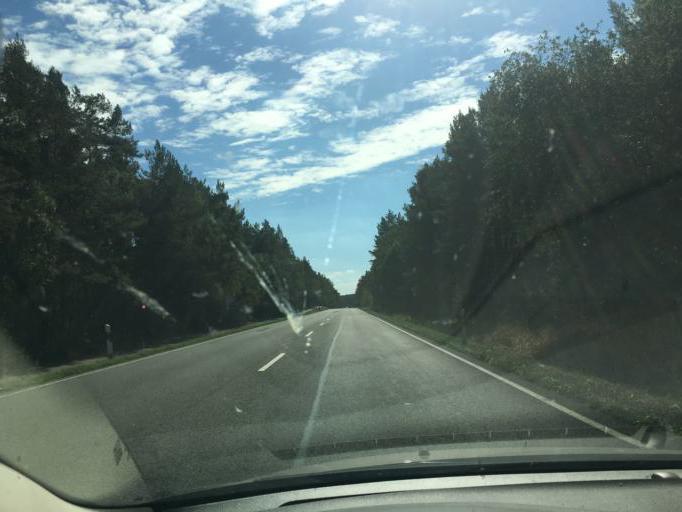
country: DE
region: Saxony-Anhalt
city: Seehausen
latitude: 52.8388
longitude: 11.7323
